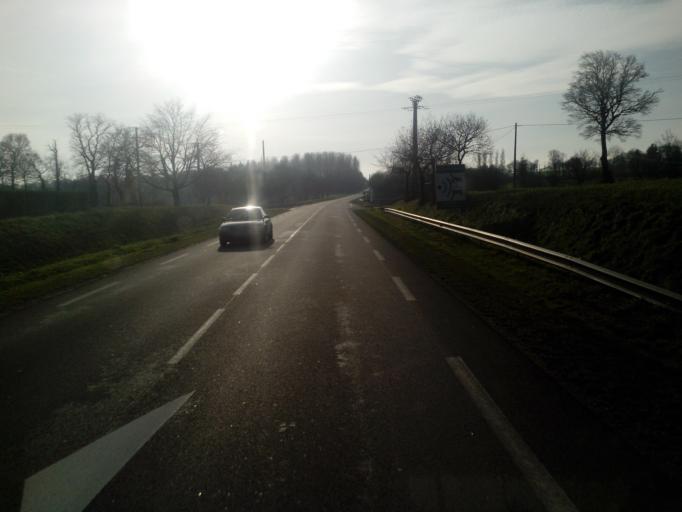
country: FR
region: Brittany
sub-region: Departement du Morbihan
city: Mauron
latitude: 48.1045
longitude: -2.2595
